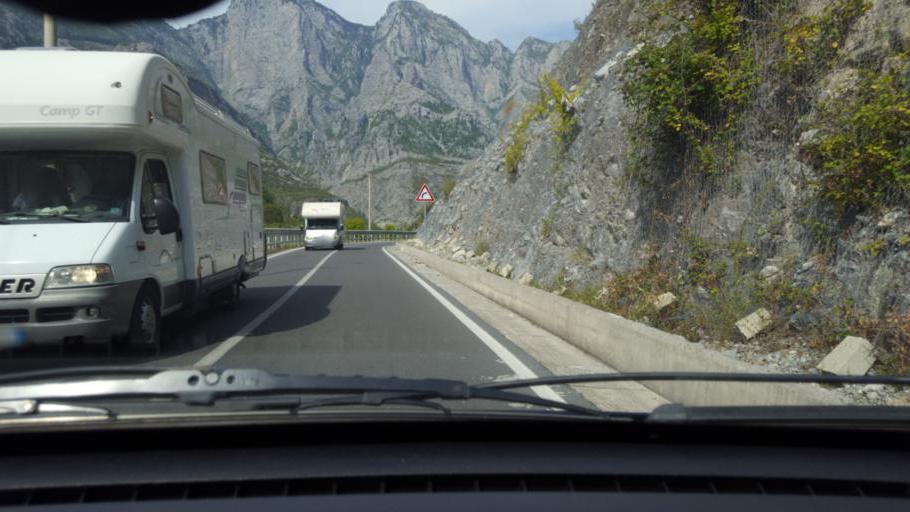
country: AL
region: Shkoder
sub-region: Rrethi i Malesia e Madhe
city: Kastrat
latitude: 42.4558
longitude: 19.5609
